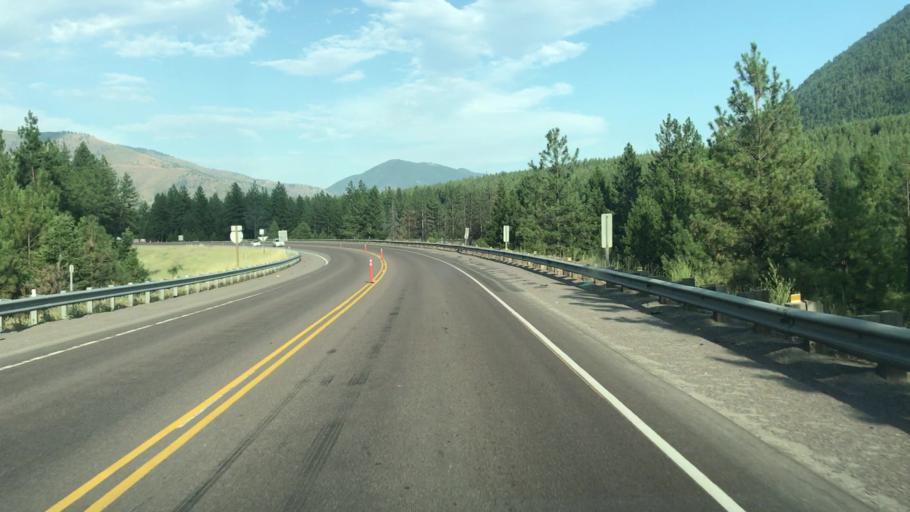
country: US
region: Montana
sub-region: Mineral County
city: Superior
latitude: 47.0176
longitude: -114.6707
